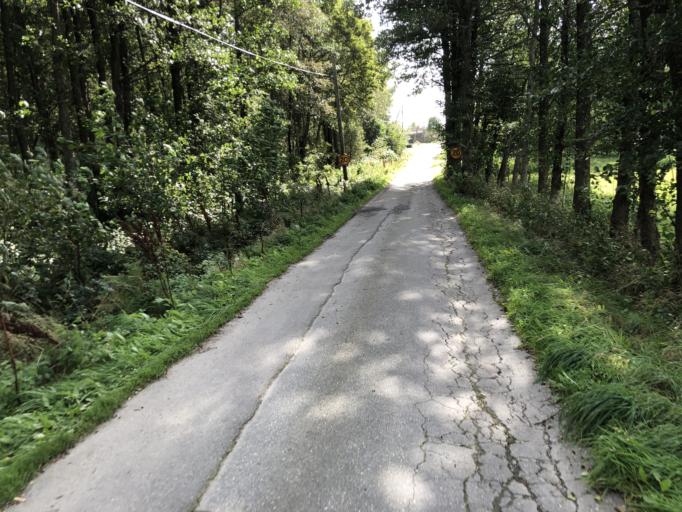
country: SE
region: Vaestra Goetaland
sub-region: Goteborg
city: Majorna
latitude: 57.7501
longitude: 11.8616
